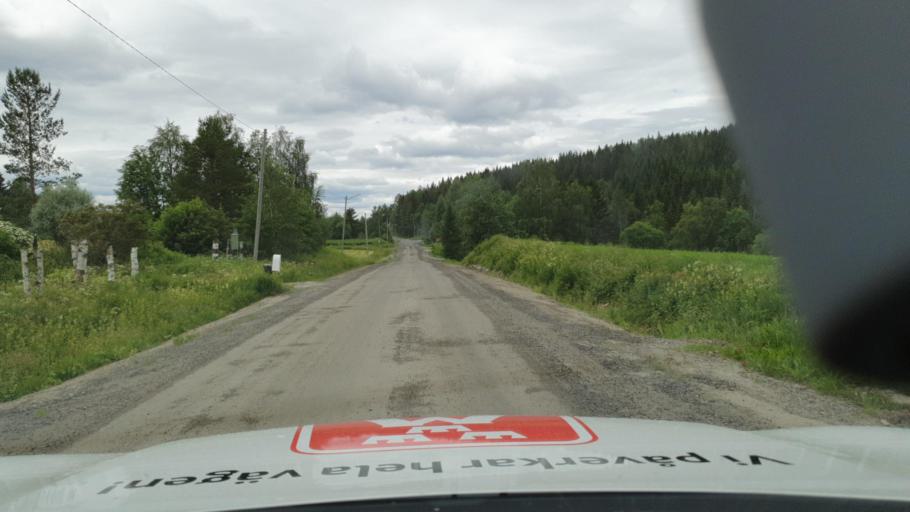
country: SE
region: Vaesterbotten
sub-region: Nordmalings Kommun
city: Nordmaling
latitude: 63.6704
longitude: 19.4387
